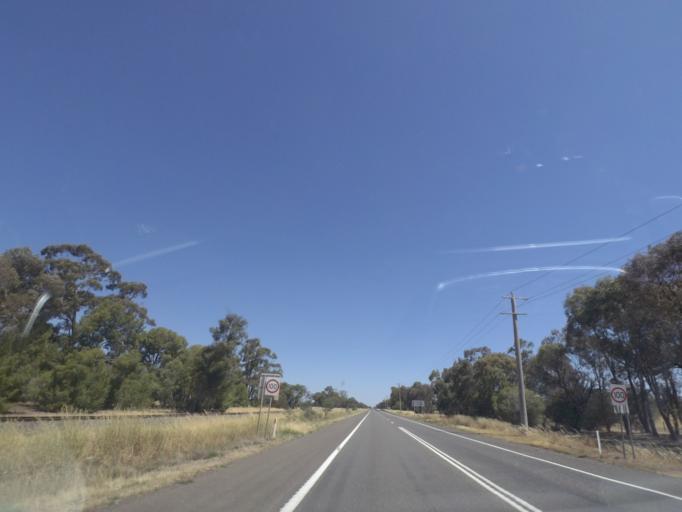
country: AU
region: Victoria
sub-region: Greater Shepparton
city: Shepparton
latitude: -36.2409
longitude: 145.4319
